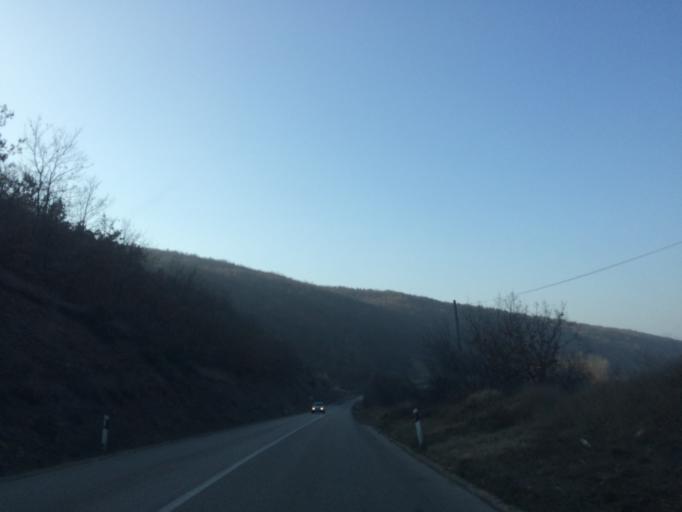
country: XK
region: Pec
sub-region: Komuna e Pejes
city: Kosuriq
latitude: 42.5081
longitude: 20.5448
